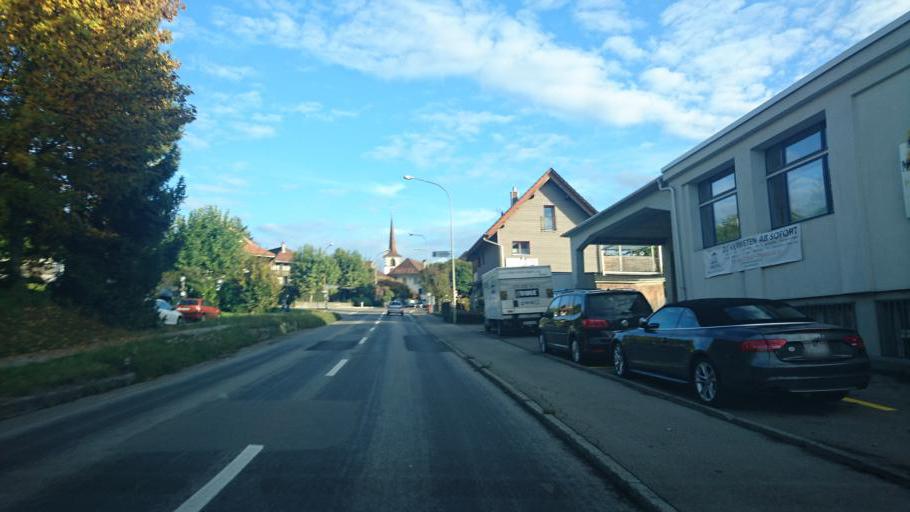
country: CH
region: Bern
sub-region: Bern-Mittelland District
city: Worb
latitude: 46.9313
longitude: 7.5619
